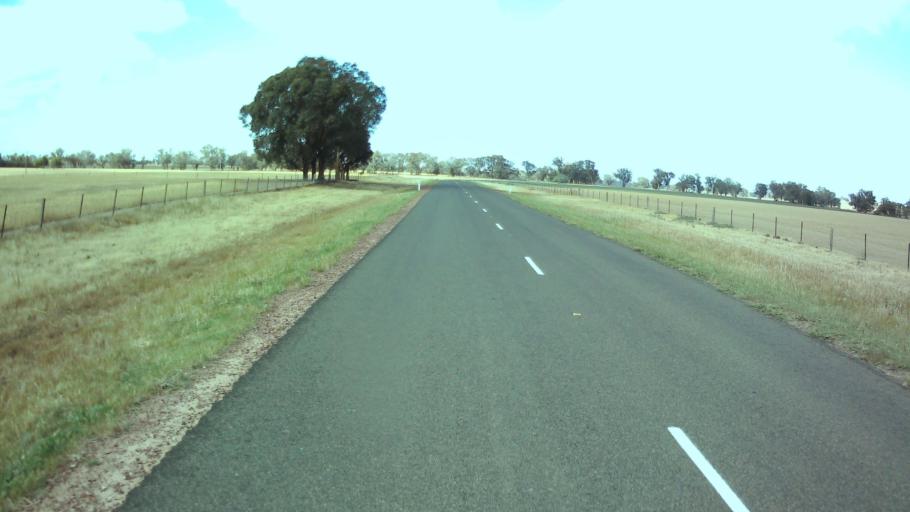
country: AU
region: New South Wales
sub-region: Weddin
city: Grenfell
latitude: -33.9606
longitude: 148.4348
